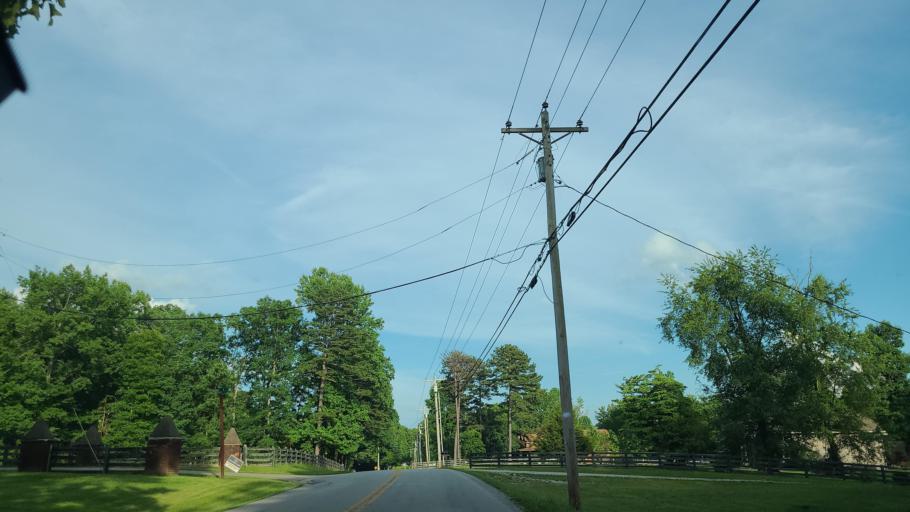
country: US
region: Kentucky
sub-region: Whitley County
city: Corbin
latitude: 36.8931
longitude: -84.2255
